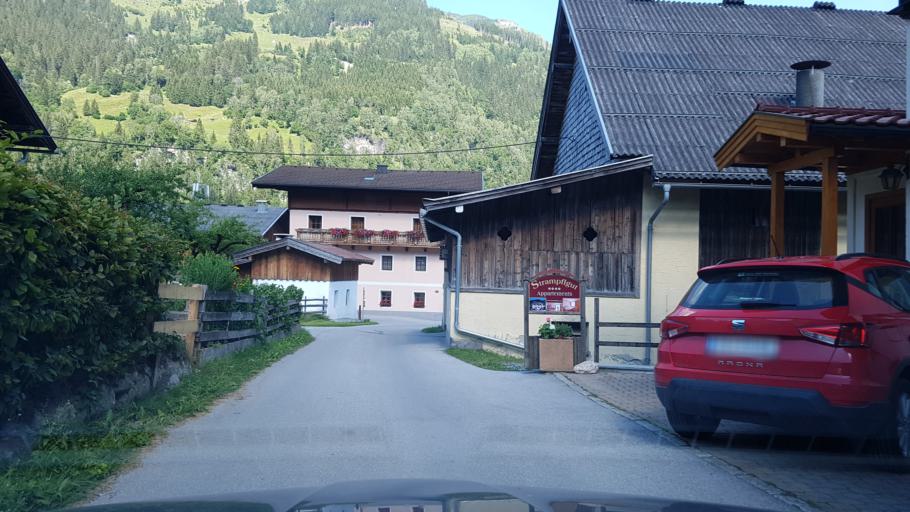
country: AT
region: Salzburg
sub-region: Politischer Bezirk Sankt Johann im Pongau
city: Dorfgastein
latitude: 47.2571
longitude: 13.0829
